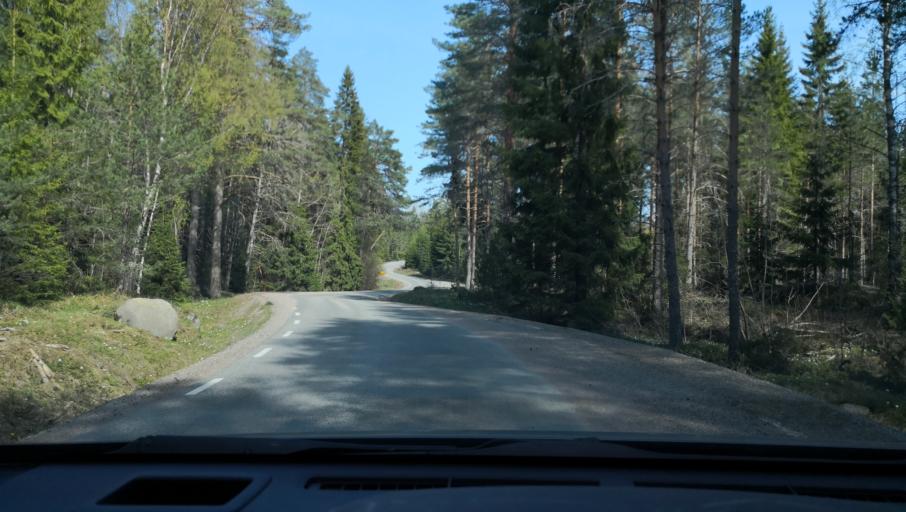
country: SE
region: Vaestmanland
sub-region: Sala Kommun
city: Sala
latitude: 60.0005
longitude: 16.6633
